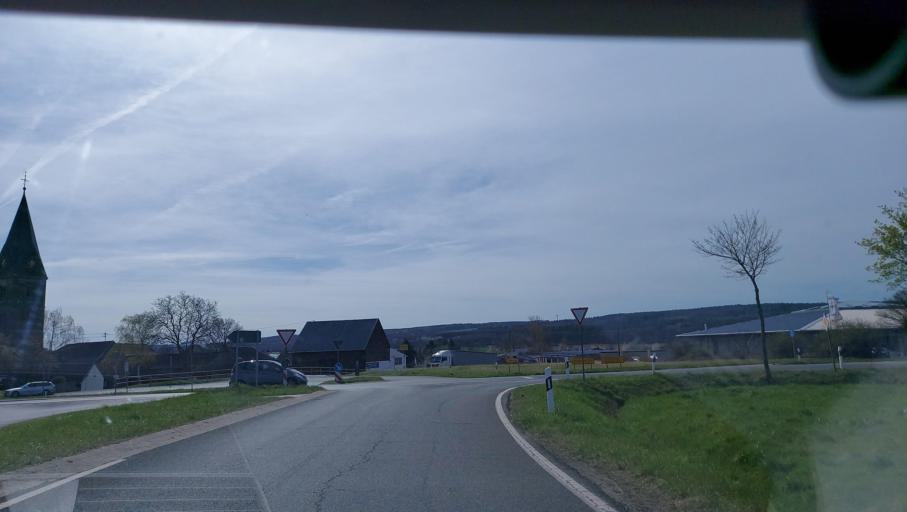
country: DE
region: North Rhine-Westphalia
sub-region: Regierungsbezirk Koln
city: Euskirchen
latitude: 50.6517
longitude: 6.7312
